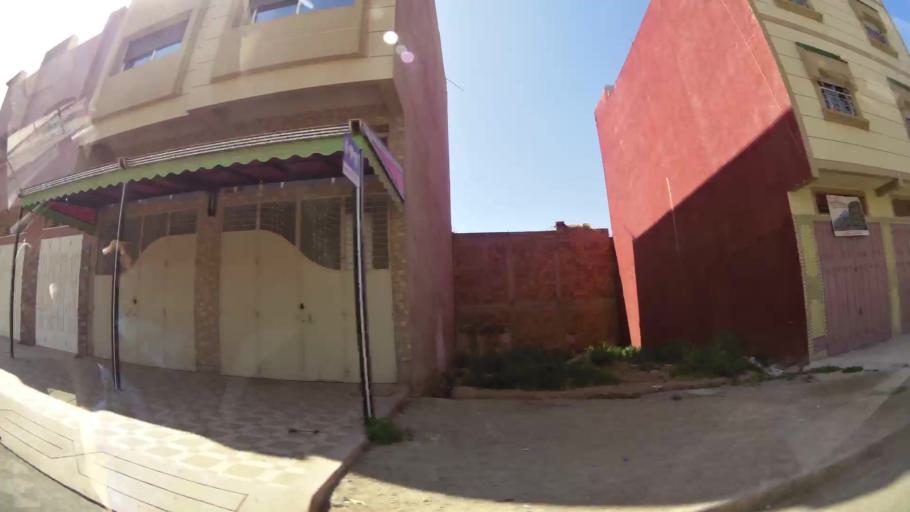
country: MA
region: Oriental
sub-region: Oujda-Angad
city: Oujda
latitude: 34.6941
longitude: -1.8775
